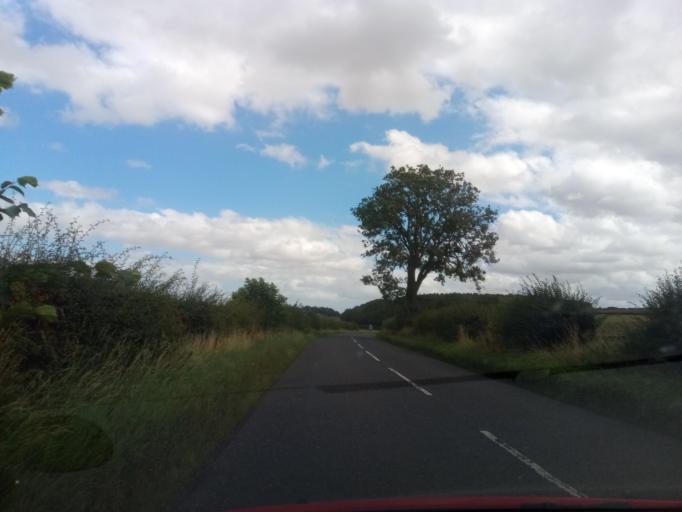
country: GB
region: Scotland
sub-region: The Scottish Borders
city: Coldstream
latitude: 55.6332
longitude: -2.3336
